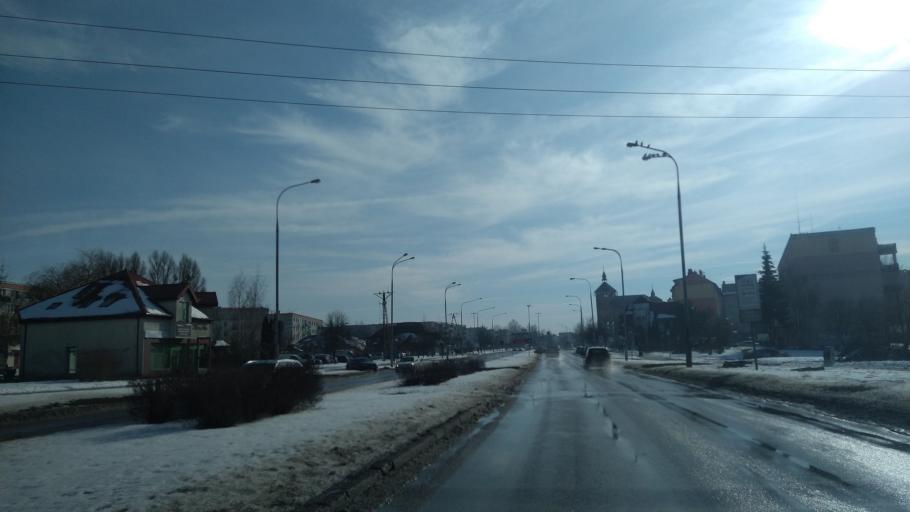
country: PL
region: Warmian-Masurian Voivodeship
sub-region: Powiat olsztynski
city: Olsztyn
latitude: 53.7446
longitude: 20.5082
